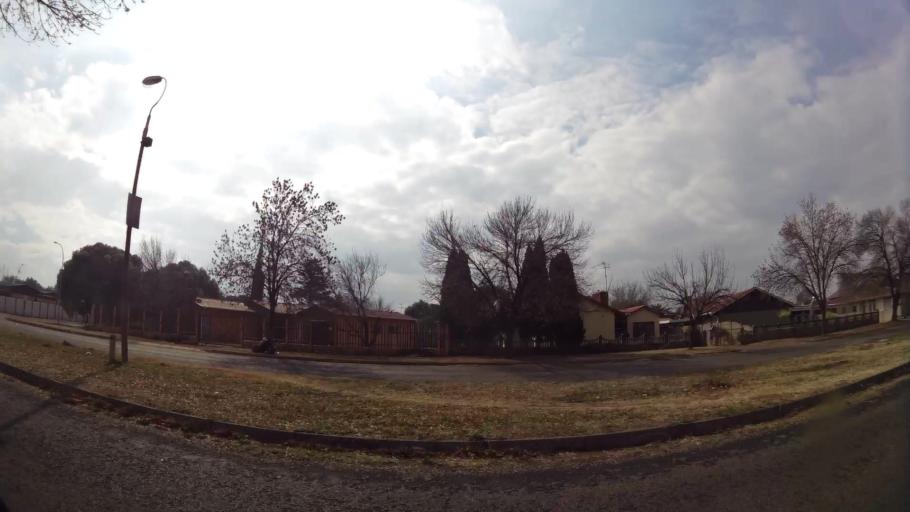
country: ZA
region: Gauteng
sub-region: Sedibeng District Municipality
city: Vanderbijlpark
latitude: -26.6896
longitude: 27.8459
